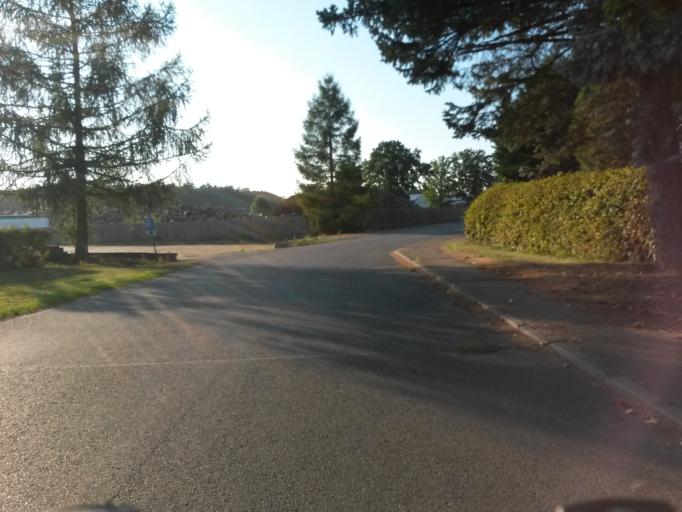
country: DE
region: Brandenburg
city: Templin
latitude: 53.1074
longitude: 13.4822
